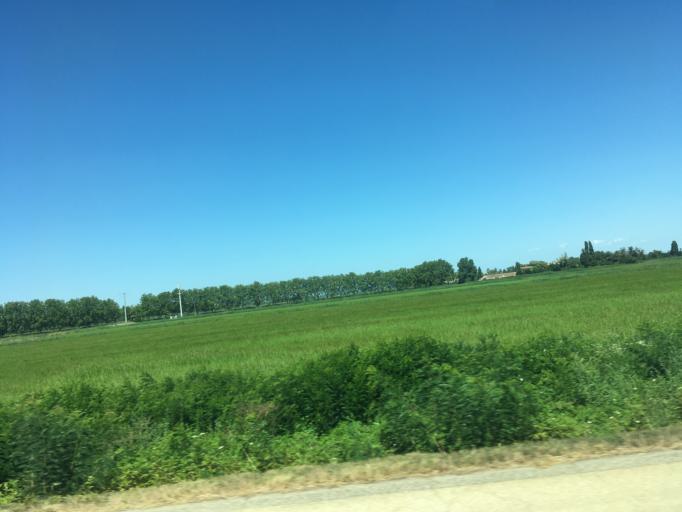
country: FR
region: Languedoc-Roussillon
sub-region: Departement du Gard
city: Saint-Gilles
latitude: 43.6131
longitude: 4.4797
